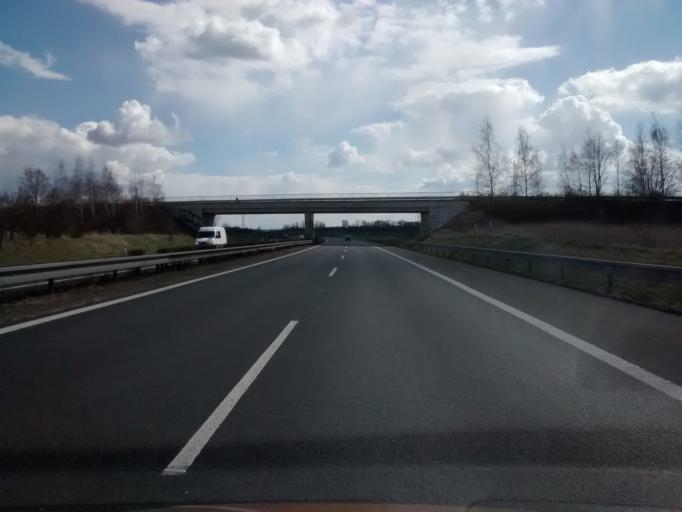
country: CZ
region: Central Bohemia
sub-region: Okres Melnik
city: Veltrusy
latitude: 50.2792
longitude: 14.3537
